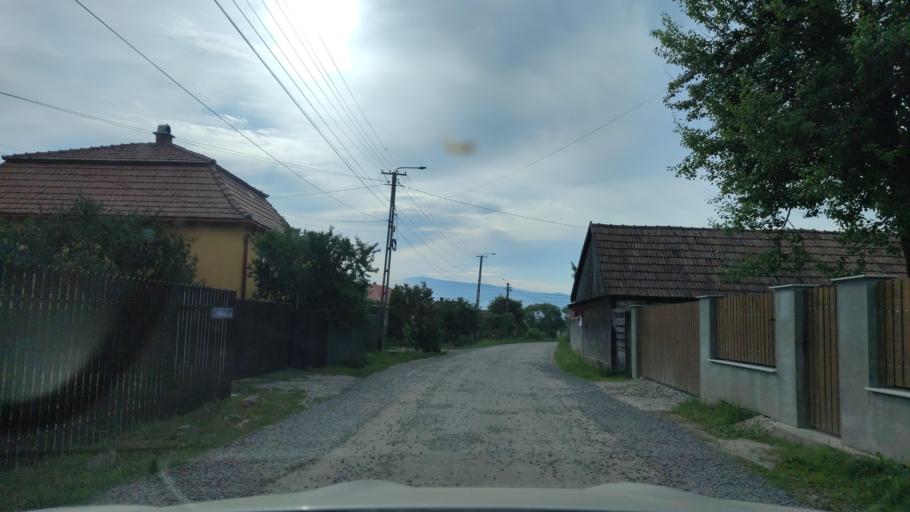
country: RO
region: Harghita
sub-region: Comuna Remetea
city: Remetea
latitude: 46.8021
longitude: 25.4569
